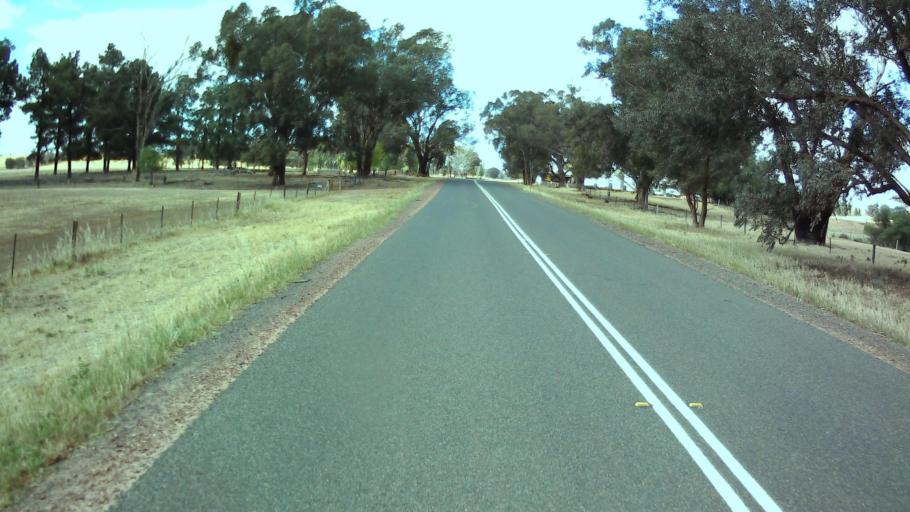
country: AU
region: New South Wales
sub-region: Weddin
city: Grenfell
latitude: -33.9529
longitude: 148.4397
